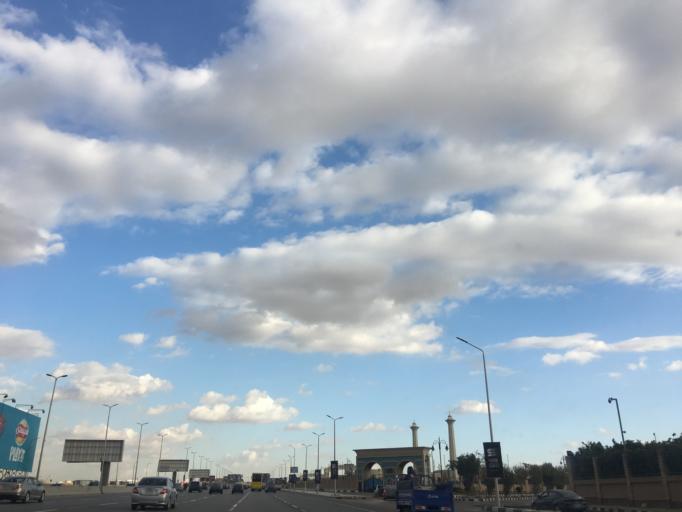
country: EG
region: Muhafazat al Qahirah
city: Cairo
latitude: 30.0206
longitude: 31.3773
